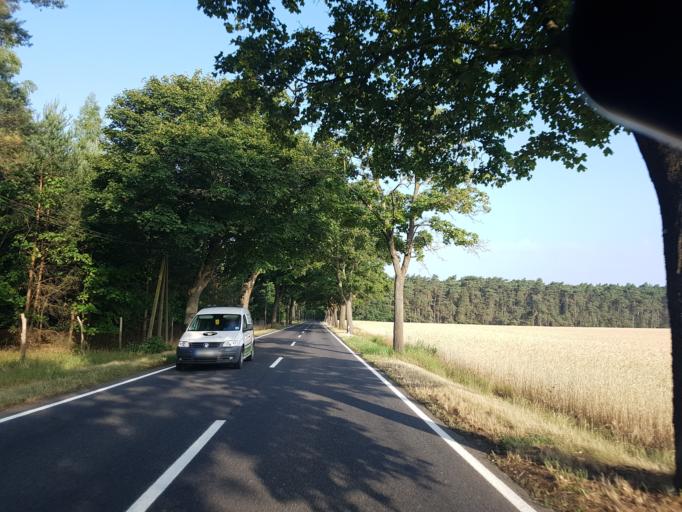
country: DE
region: Brandenburg
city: Ihlow
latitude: 51.8102
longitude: 13.2635
